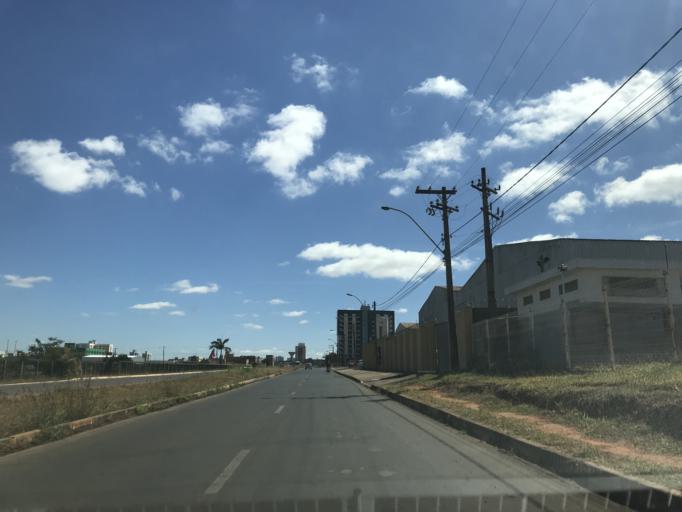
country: BR
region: Federal District
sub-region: Brasilia
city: Brasilia
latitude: -15.8754
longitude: -48.0242
